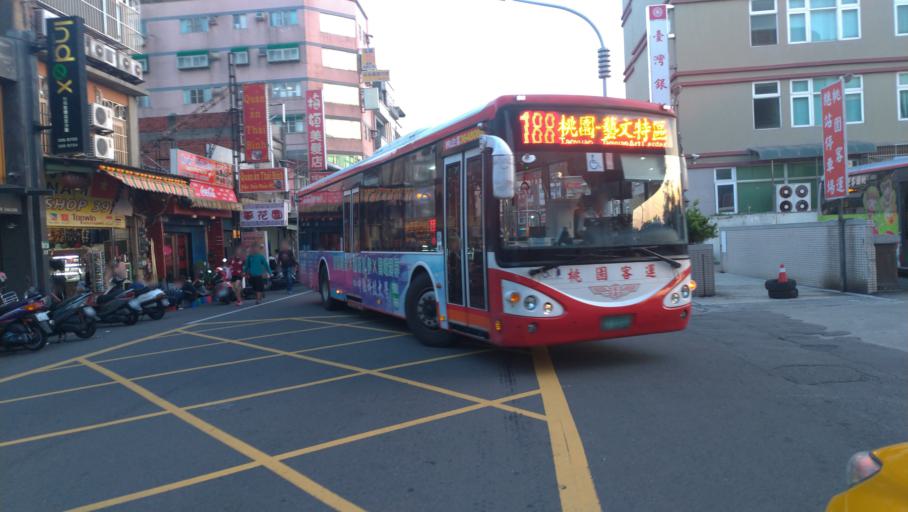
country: TW
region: Taiwan
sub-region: Taoyuan
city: Taoyuan
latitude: 24.9867
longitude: 121.3142
